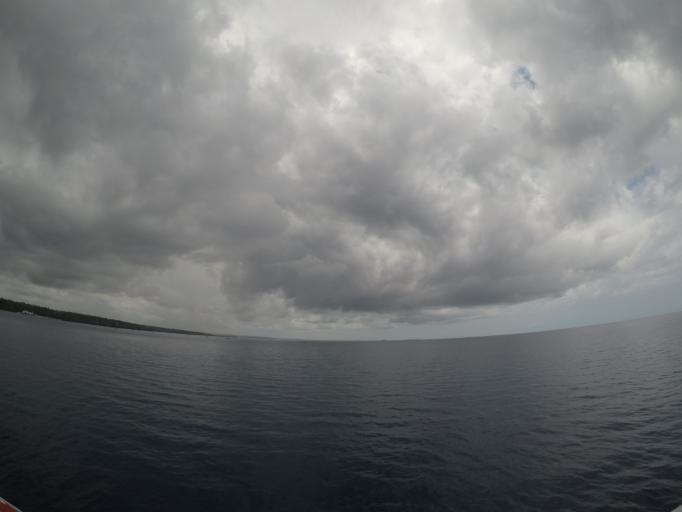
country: TZ
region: Zanzibar North
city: Mkokotoni
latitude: -5.9861
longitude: 39.1739
